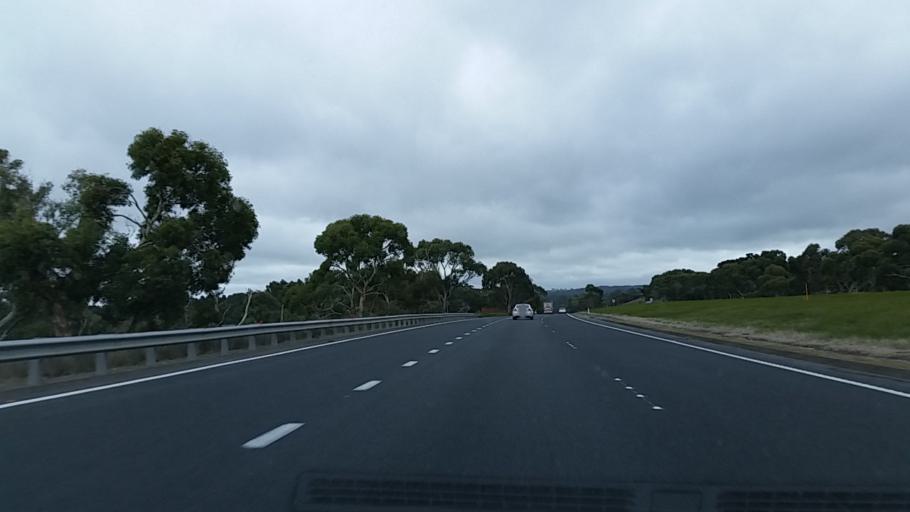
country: AU
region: South Australia
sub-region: Mount Barker
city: Nairne
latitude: -35.0576
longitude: 138.9092
